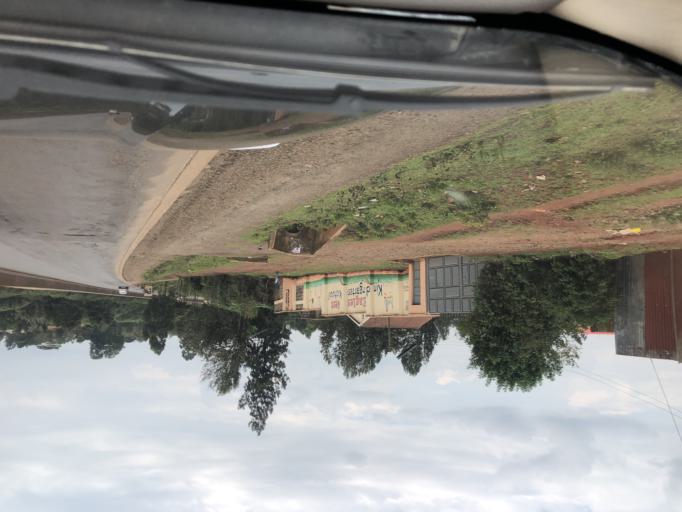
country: KE
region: Kiambu
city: Kikuyu
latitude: -1.2255
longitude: 36.6639
